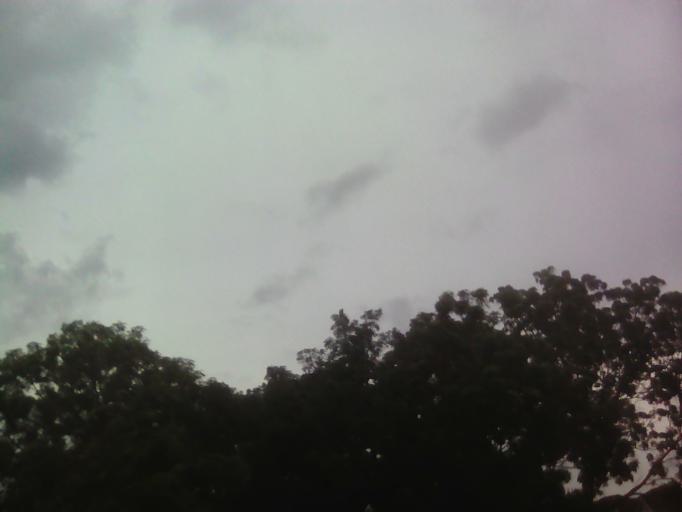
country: MY
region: Penang
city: Butterworth
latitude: 5.4058
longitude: 100.3848
